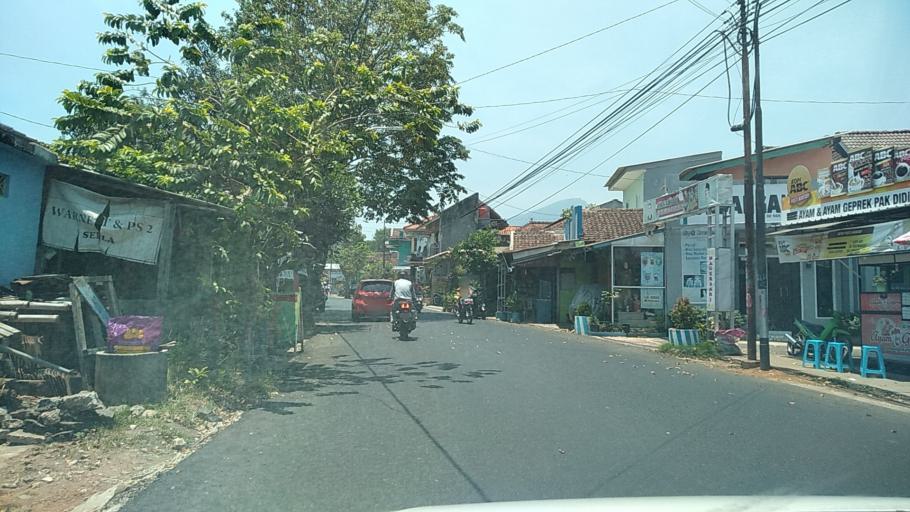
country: ID
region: Central Java
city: Ungaran
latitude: -7.0857
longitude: 110.3615
